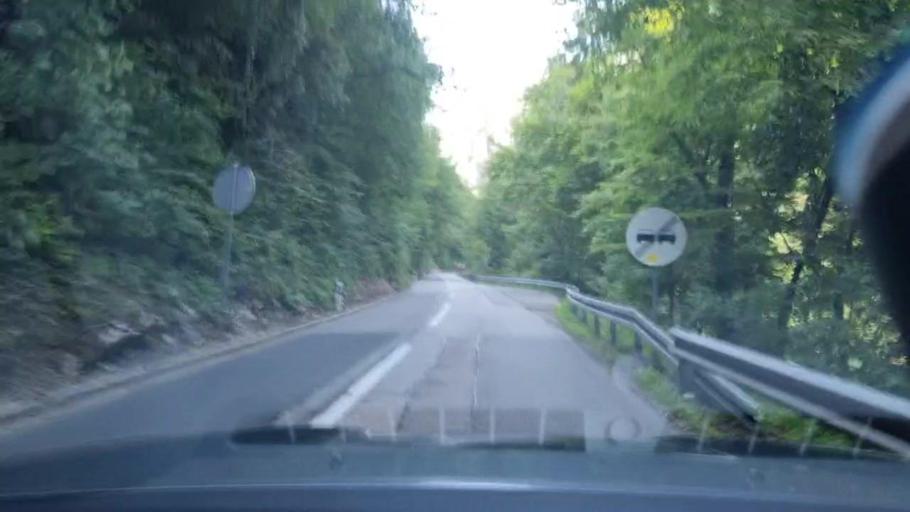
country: BA
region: Federation of Bosnia and Herzegovina
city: Stijena
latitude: 44.8778
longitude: 16.0716
